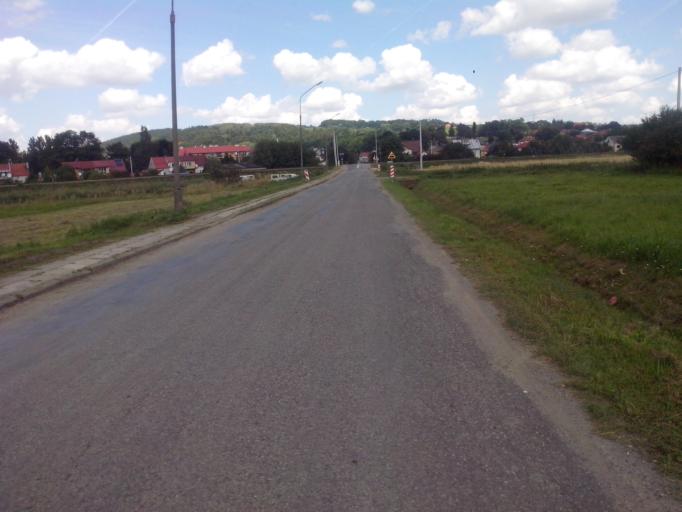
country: PL
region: Subcarpathian Voivodeship
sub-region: Powiat strzyzowski
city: Strzyzow
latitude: 49.8675
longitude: 21.7711
